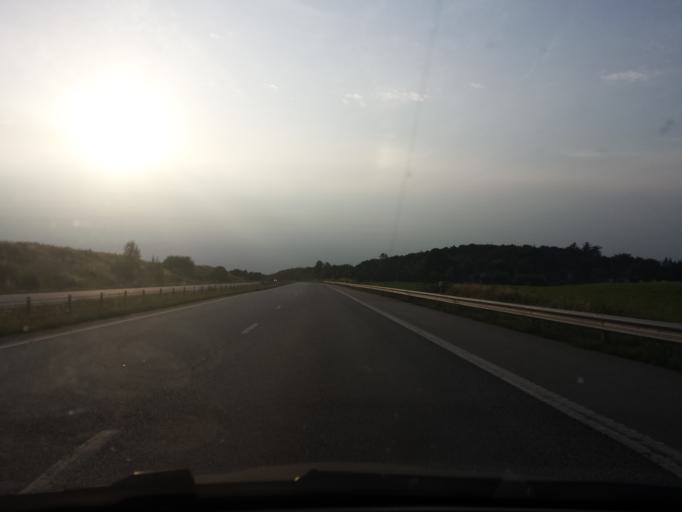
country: SE
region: Skane
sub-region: Svedala Kommun
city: Svedala
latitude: 55.5224
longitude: 13.2313
